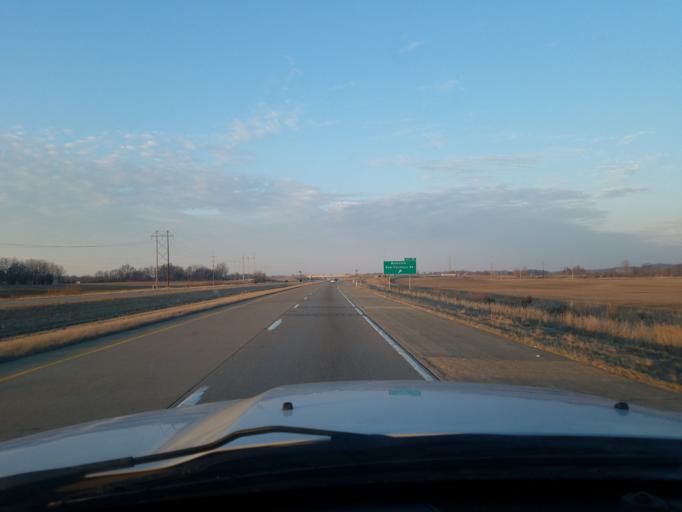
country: US
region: Indiana
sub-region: Vanderburgh County
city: Melody Hill
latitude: 38.0820
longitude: -87.4767
